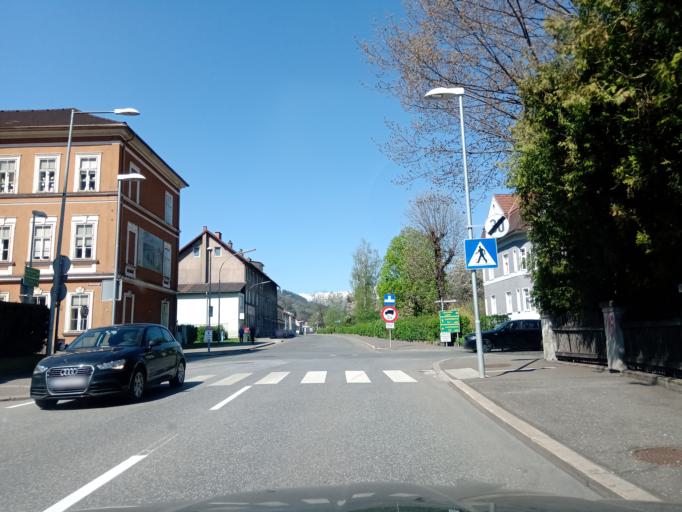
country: AT
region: Styria
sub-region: Politischer Bezirk Leoben
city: Leoben
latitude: 47.3762
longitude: 15.0725
